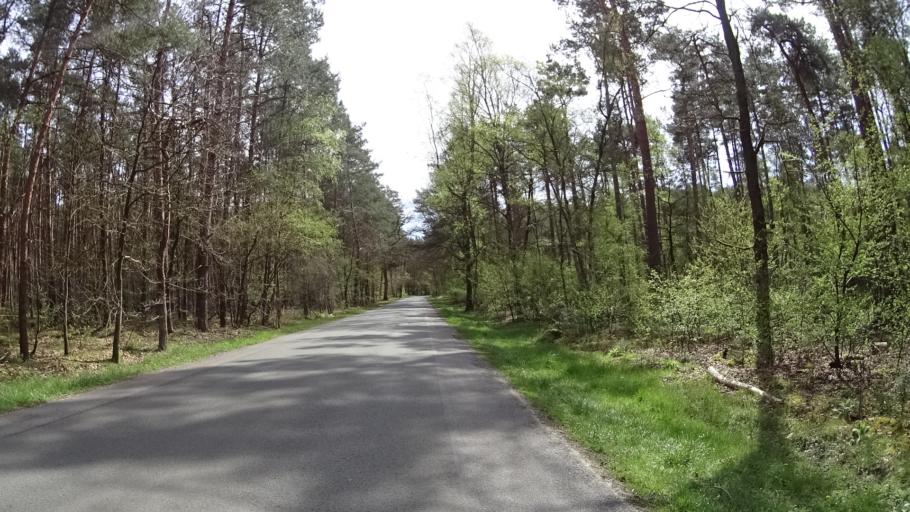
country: DE
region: Lower Saxony
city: Emsburen
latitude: 52.4369
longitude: 7.3481
